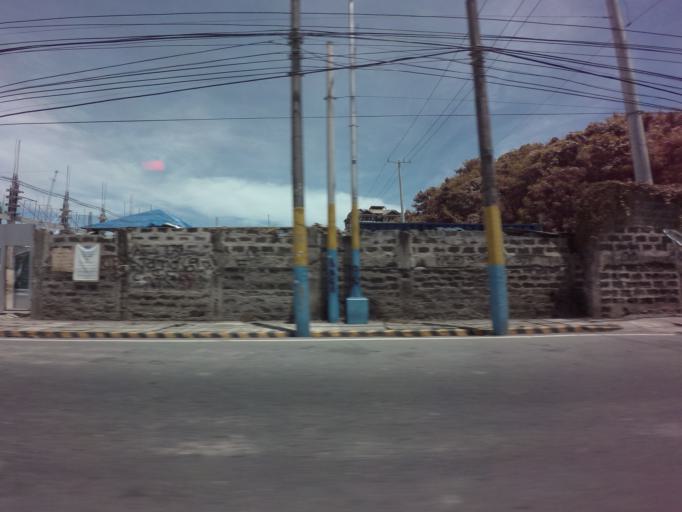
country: PH
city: Sambayanihan People's Village
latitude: 14.4514
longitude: 121.0505
